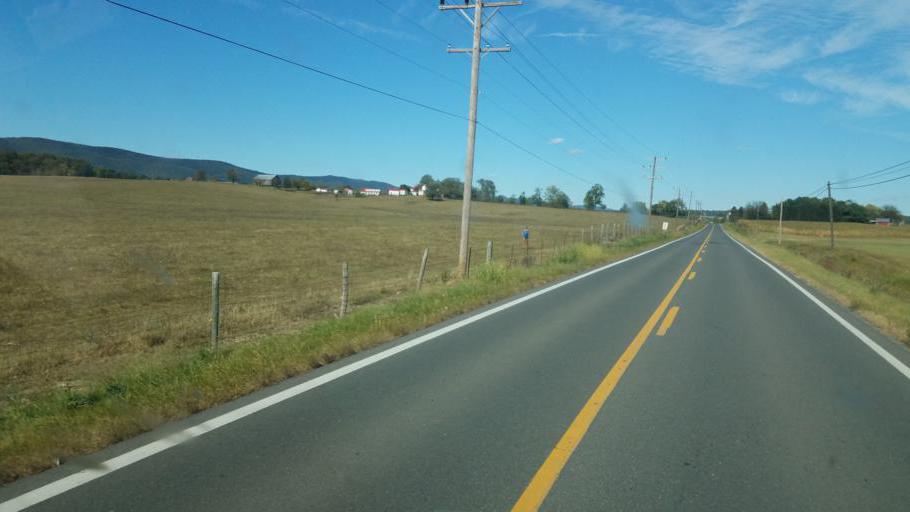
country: US
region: Virginia
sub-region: Page County
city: Luray
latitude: 38.7131
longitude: -78.4317
